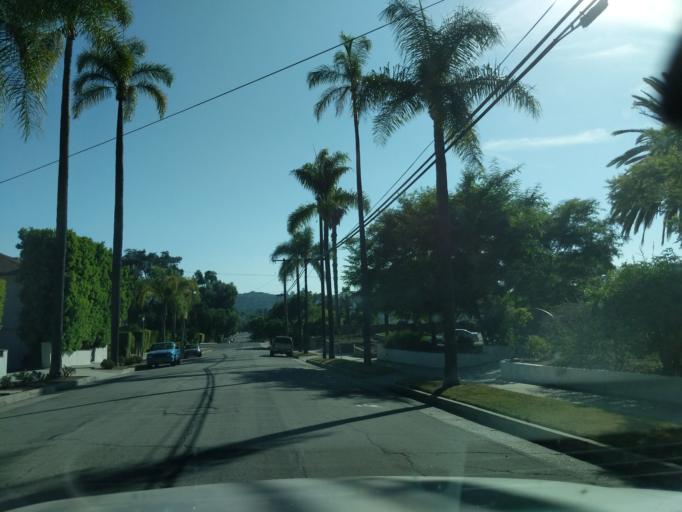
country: US
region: California
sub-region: Santa Barbara County
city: Mission Canyon
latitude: 34.4337
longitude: -119.7139
